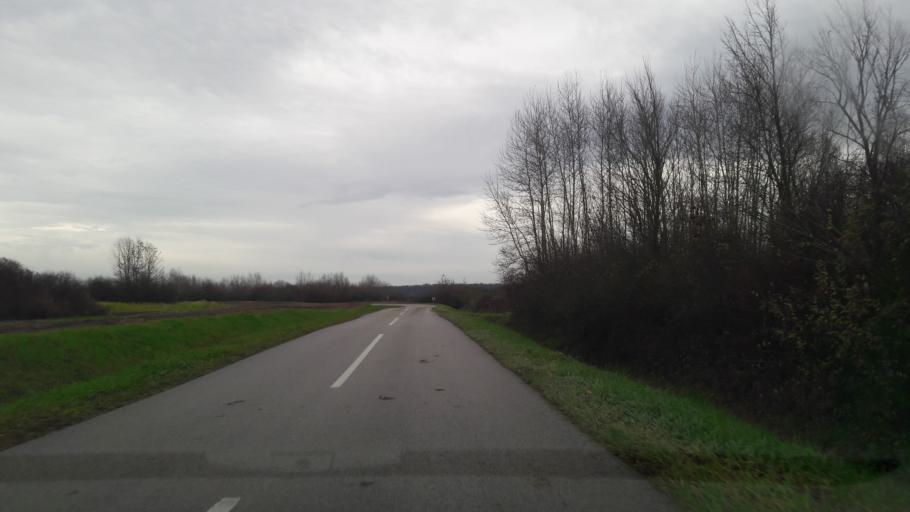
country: HR
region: Osjecko-Baranjska
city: Velimirovac
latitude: 45.6344
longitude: 18.1088
